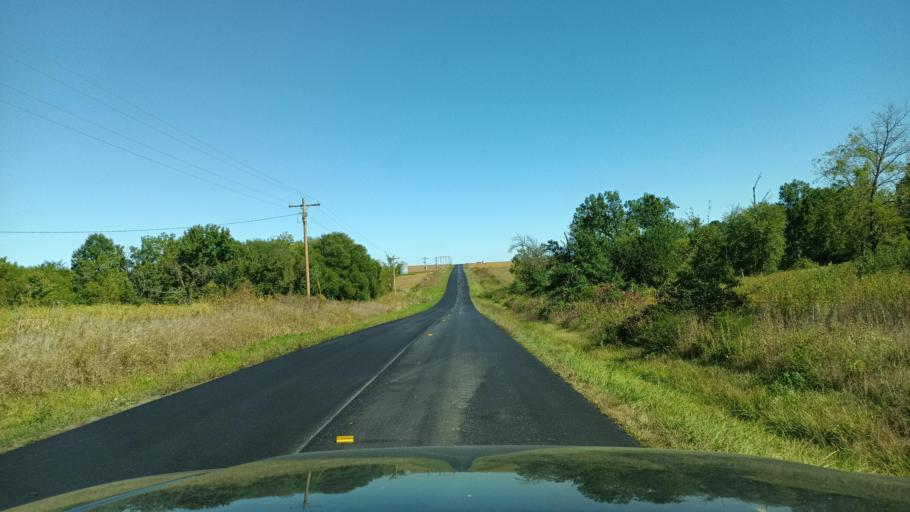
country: US
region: Missouri
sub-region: Macon County
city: La Plata
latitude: 39.9279
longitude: -92.5646
